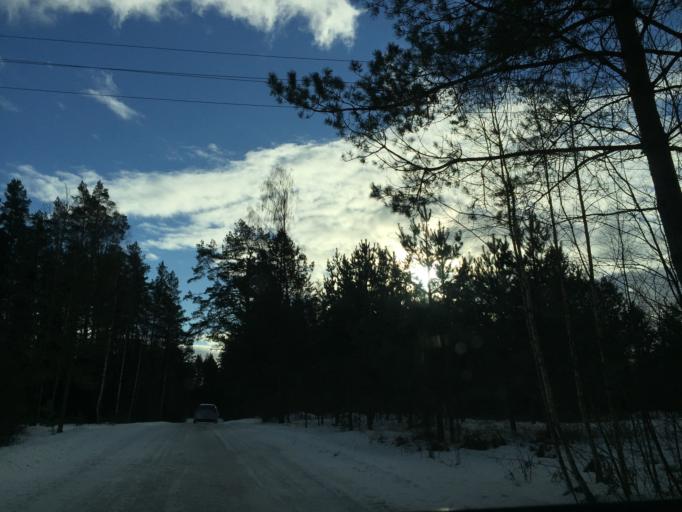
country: LV
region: Lielvarde
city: Lielvarde
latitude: 56.5655
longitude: 24.7975
